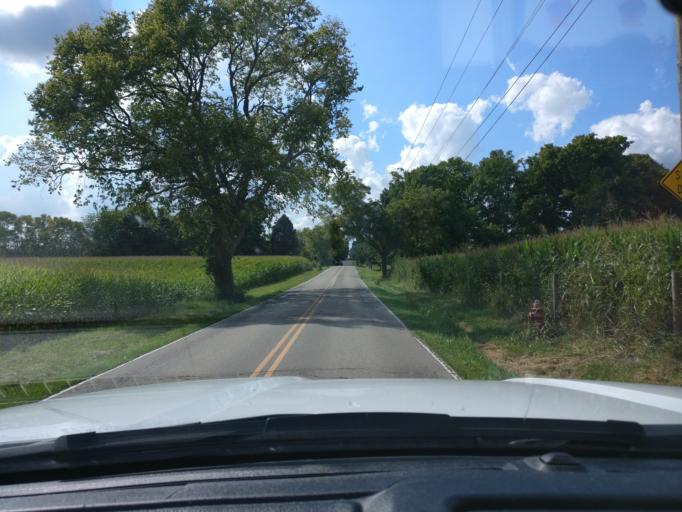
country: US
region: Ohio
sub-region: Warren County
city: Springboro
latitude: 39.5052
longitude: -84.2205
